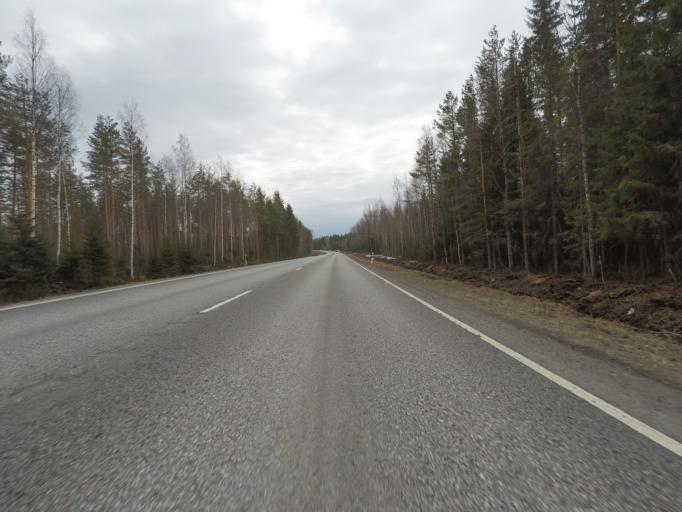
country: FI
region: Central Finland
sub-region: Jyvaeskylae
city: Toivakka
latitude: 62.2224
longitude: 26.2021
